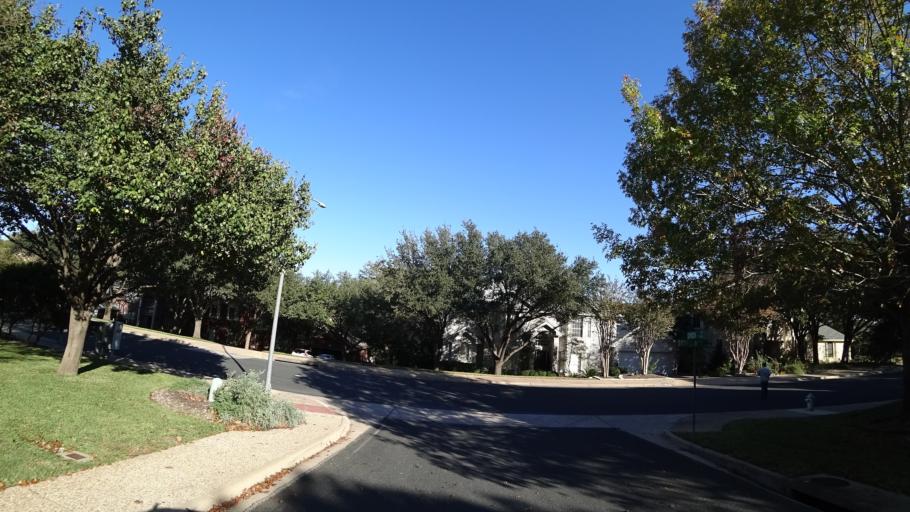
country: US
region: Texas
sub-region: Williamson County
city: Jollyville
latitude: 30.4154
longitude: -97.7756
